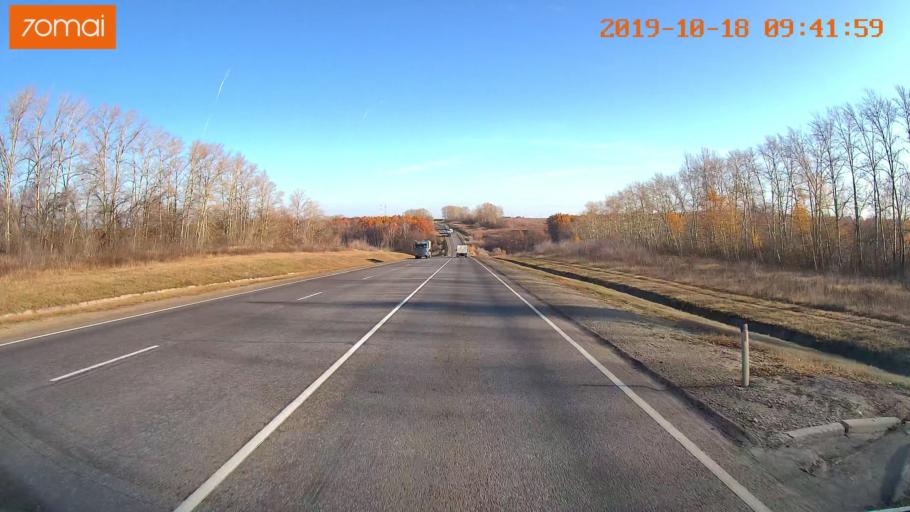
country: RU
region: Tula
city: Kazachka
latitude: 53.2815
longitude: 38.1701
